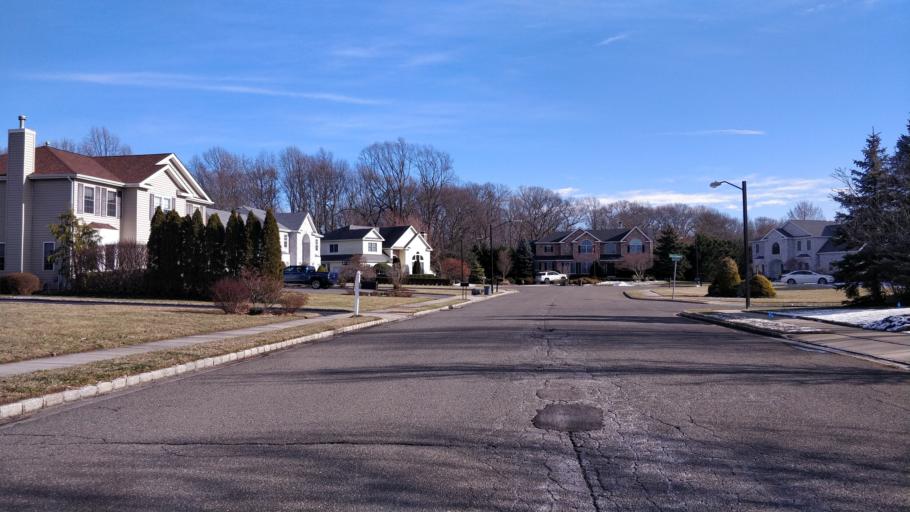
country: US
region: New York
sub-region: Nassau County
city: Oyster Bay
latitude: 40.8553
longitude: -73.5224
